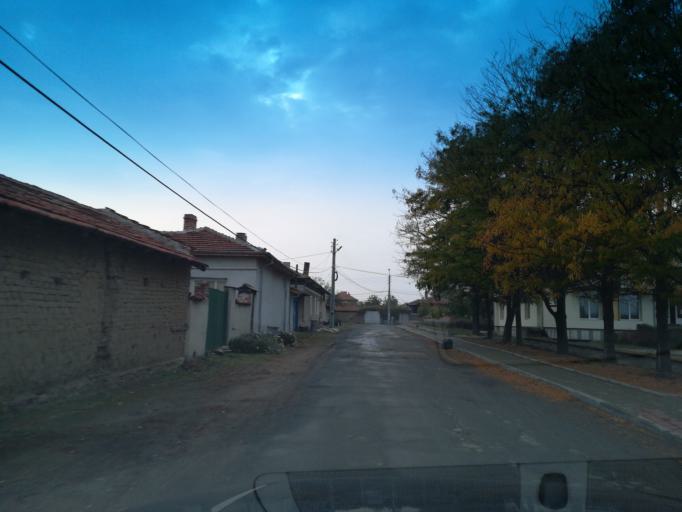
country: BG
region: Stara Zagora
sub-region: Obshtina Chirpan
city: Chirpan
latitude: 42.1748
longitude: 25.2092
